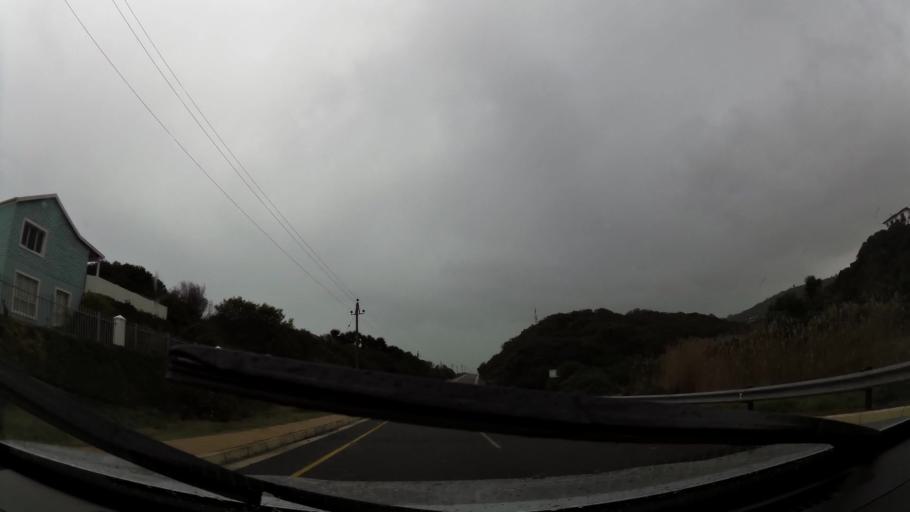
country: ZA
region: Western Cape
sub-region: Eden District Municipality
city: Mossel Bay
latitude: -34.0494
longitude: 22.2838
